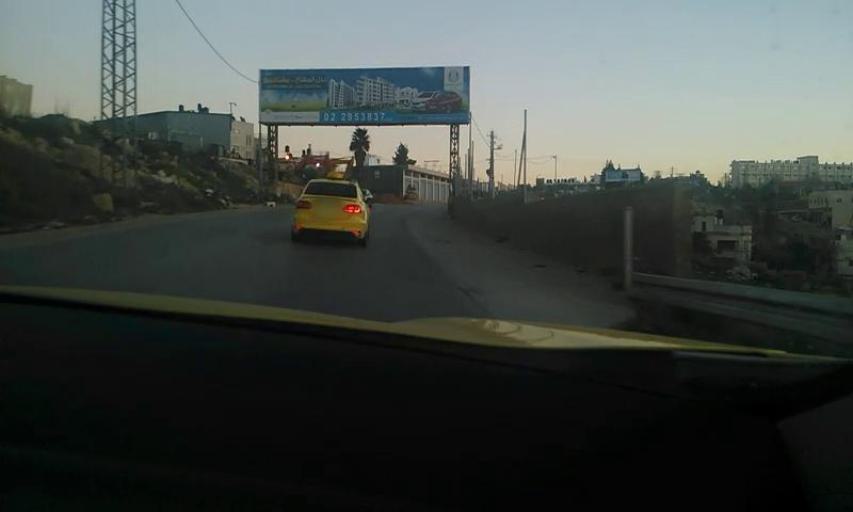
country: PS
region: West Bank
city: Jifna
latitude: 31.9481
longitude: 35.2157
